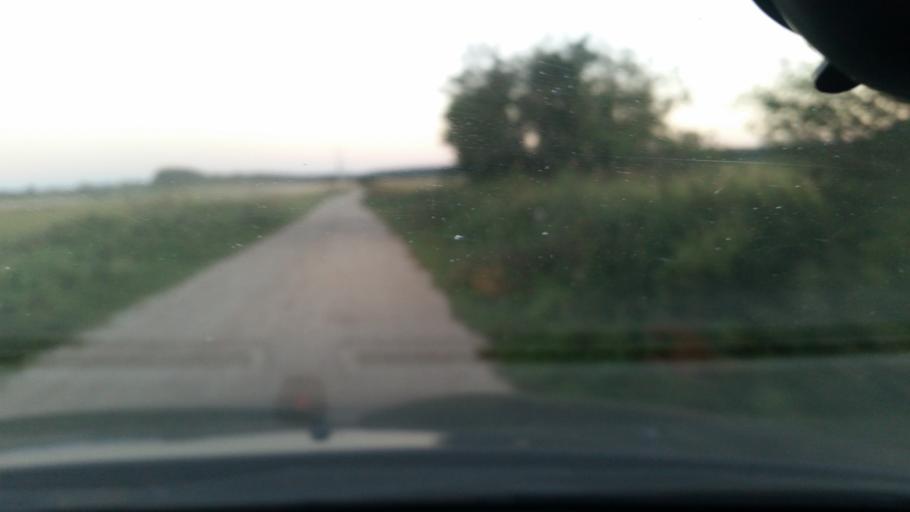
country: PL
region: Pomeranian Voivodeship
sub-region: Powiat wejherowski
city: Choczewo
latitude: 54.7823
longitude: 17.7936
